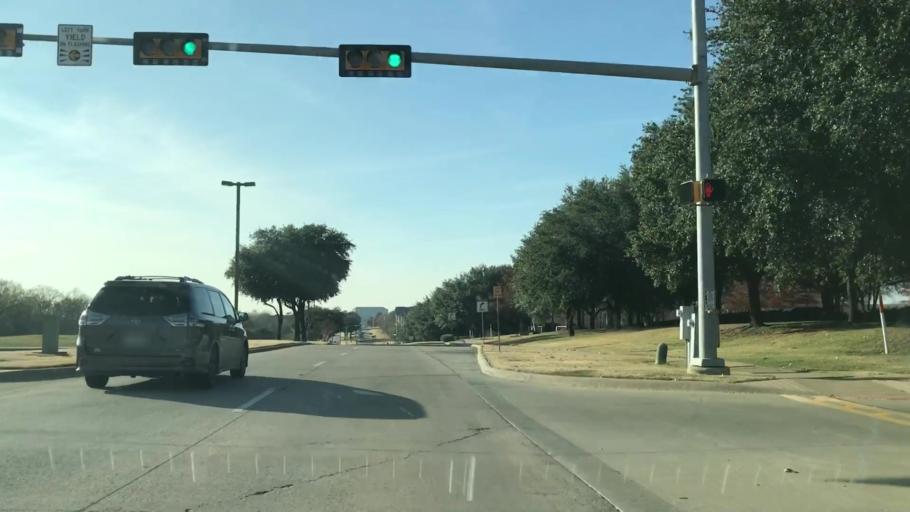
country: US
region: Texas
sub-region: Dallas County
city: Farmers Branch
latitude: 32.8959
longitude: -96.9484
